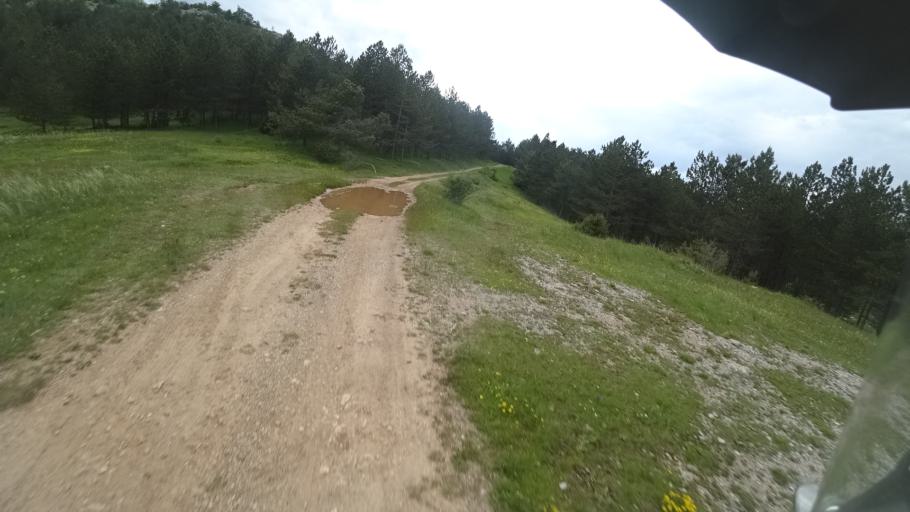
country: HR
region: Zadarska
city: Obrovac
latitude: 44.2753
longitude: 15.7394
